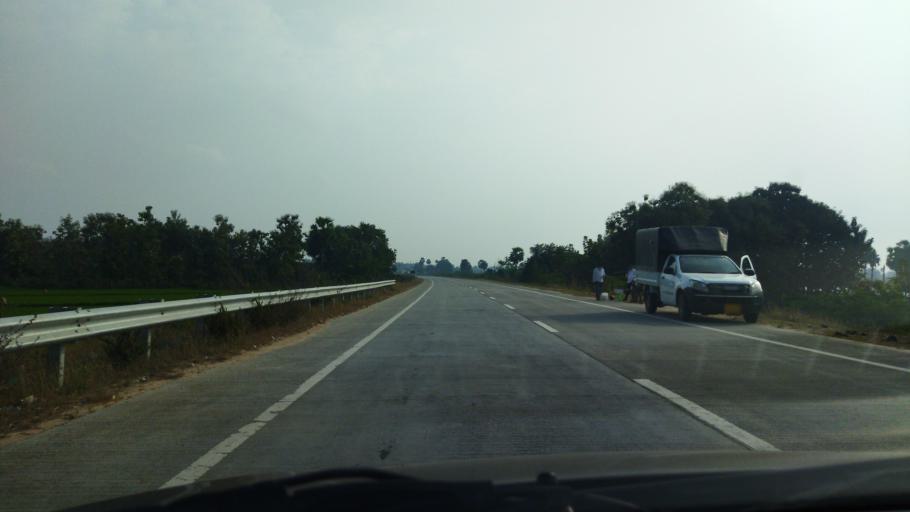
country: IN
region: Telangana
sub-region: Nalgonda
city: Nalgonda
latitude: 17.1789
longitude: 79.4066
